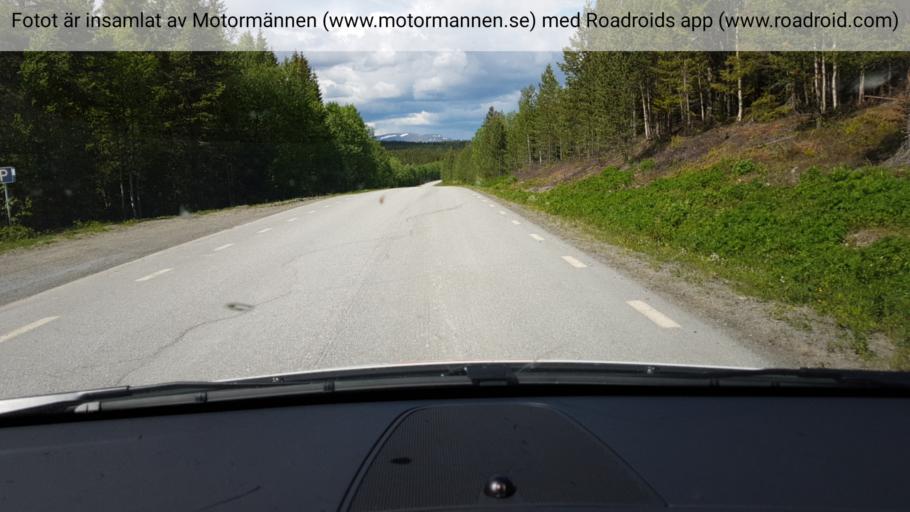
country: SE
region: Jaemtland
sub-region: Bergs Kommun
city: Hoverberg
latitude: 63.0324
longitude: 14.0484
